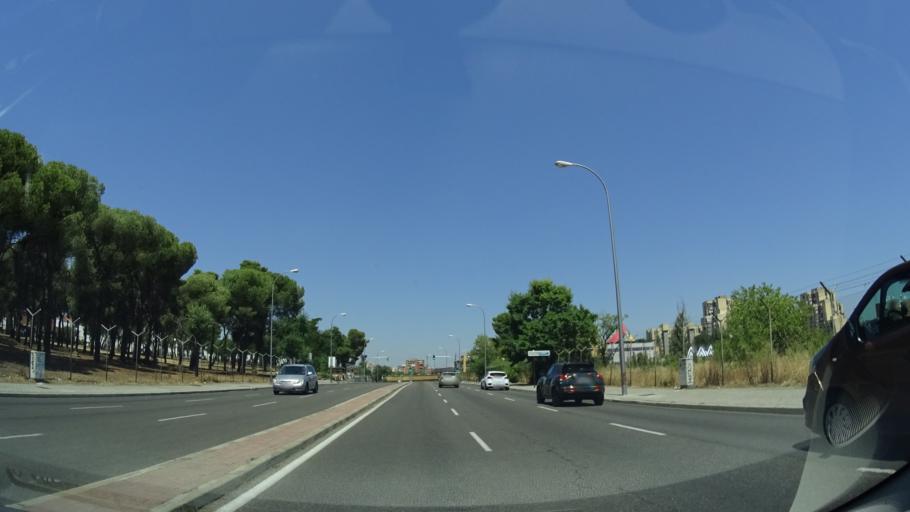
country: ES
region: Madrid
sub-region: Provincia de Madrid
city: Latina
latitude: 40.3810
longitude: -3.7571
